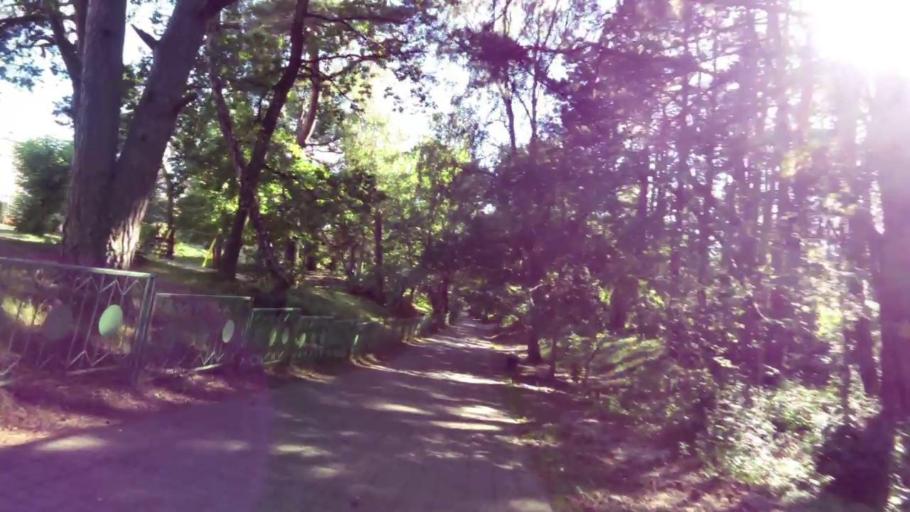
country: PL
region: West Pomeranian Voivodeship
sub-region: Powiat slawienski
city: Darlowo
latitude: 54.3788
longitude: 16.3110
